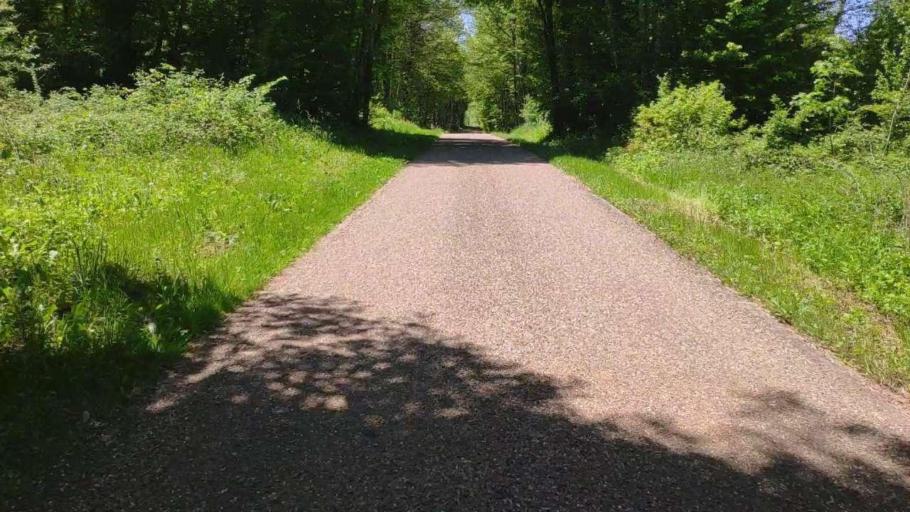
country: FR
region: Franche-Comte
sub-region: Departement du Jura
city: Poligny
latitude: 46.7344
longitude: 5.6737
